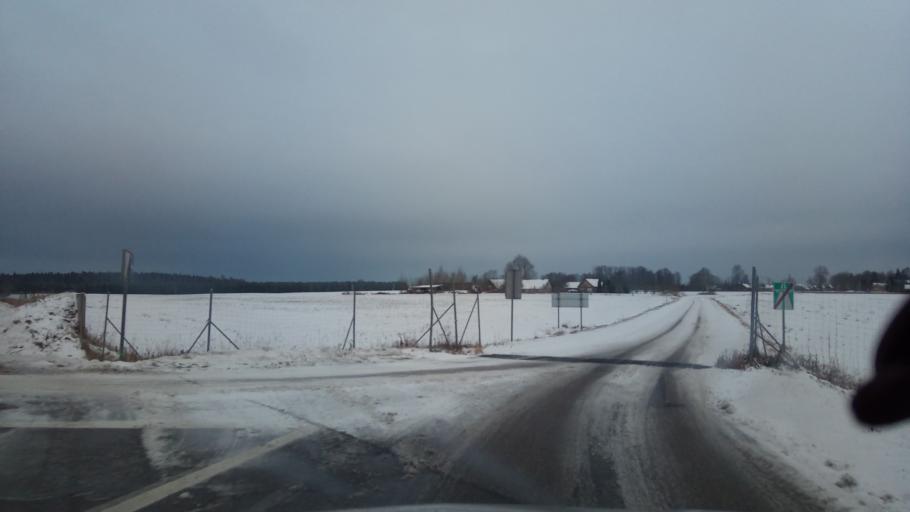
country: LT
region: Vilnius County
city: Ukmerge
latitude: 55.5011
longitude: 24.6169
